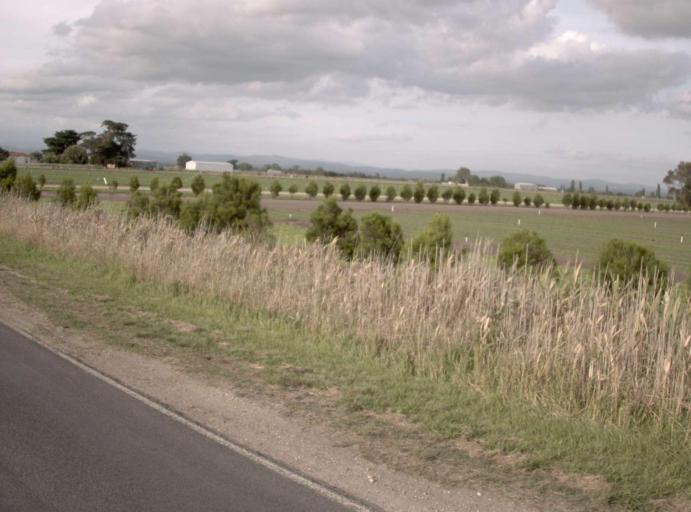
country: AU
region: Victoria
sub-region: Wellington
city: Sale
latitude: -37.9046
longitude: 146.9942
